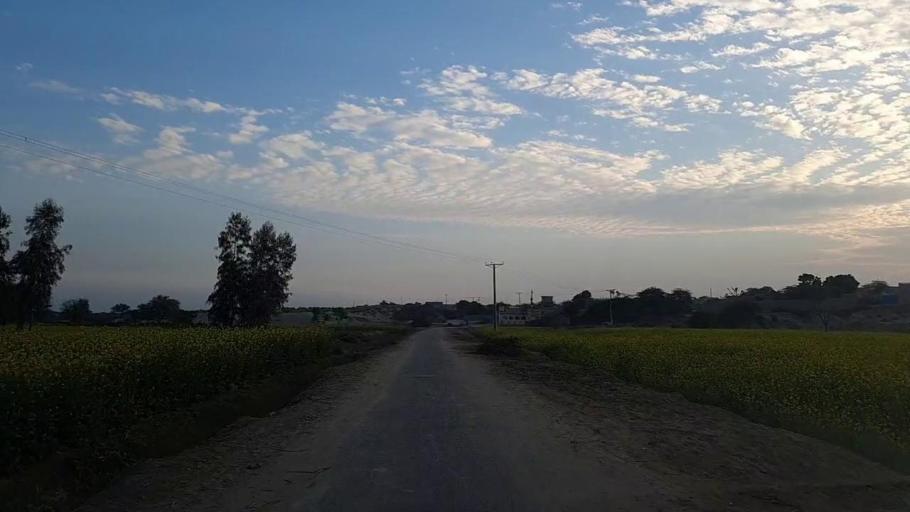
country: PK
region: Sindh
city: Daur
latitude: 26.4142
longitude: 68.4678
